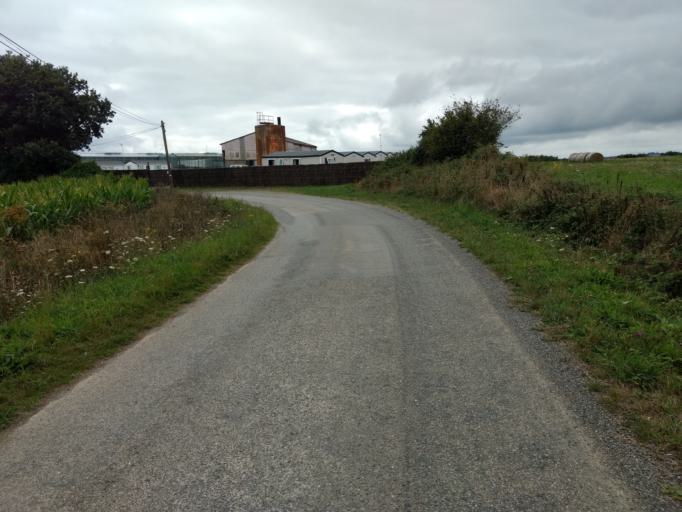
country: FR
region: Brittany
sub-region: Departement du Finistere
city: Loperhet
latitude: 48.3633
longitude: -4.2909
